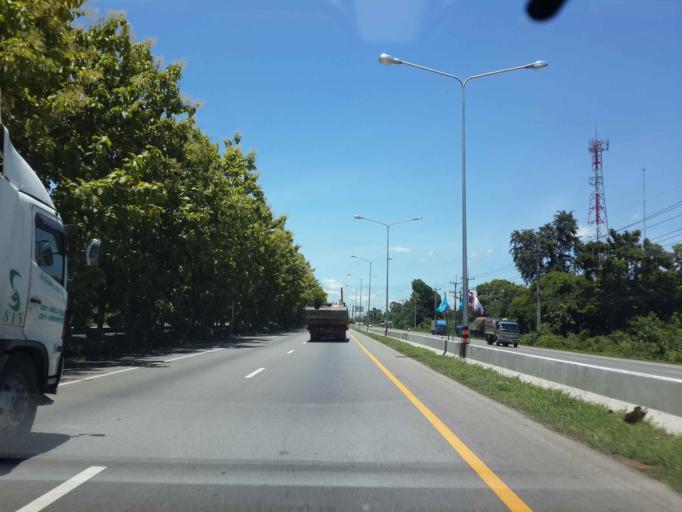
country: TH
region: Phetchaburi
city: Khao Yoi
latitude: 13.1502
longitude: 99.8526
